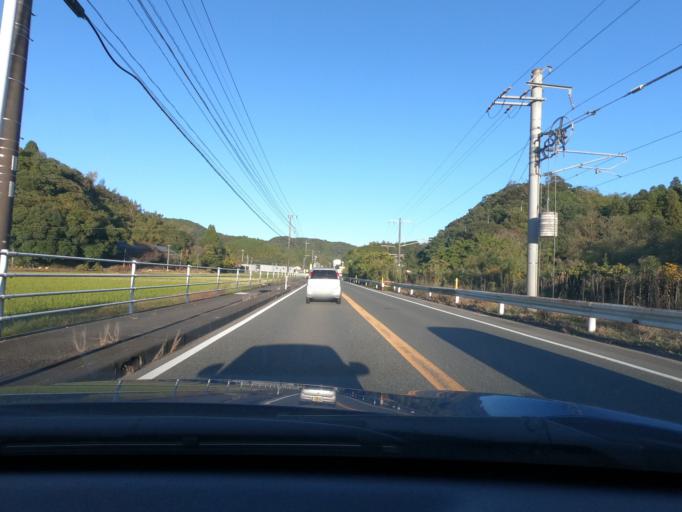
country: JP
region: Kagoshima
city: Satsumasendai
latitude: 31.8481
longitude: 130.2589
